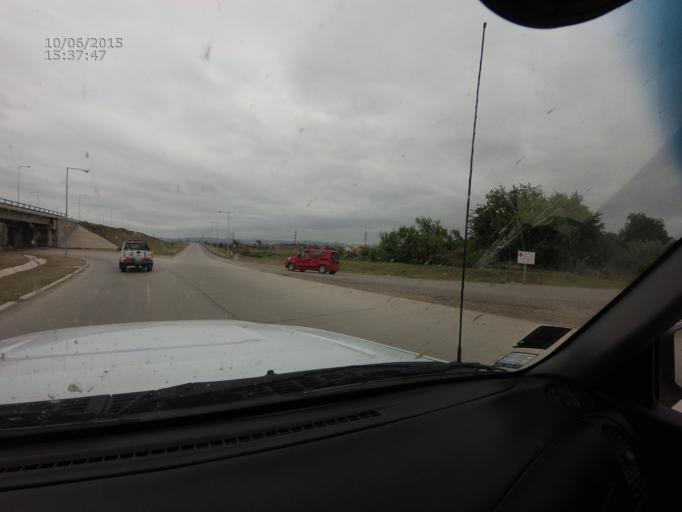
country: AR
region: Cordoba
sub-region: Departamento de Capital
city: Cordoba
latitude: -31.3529
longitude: -64.2258
